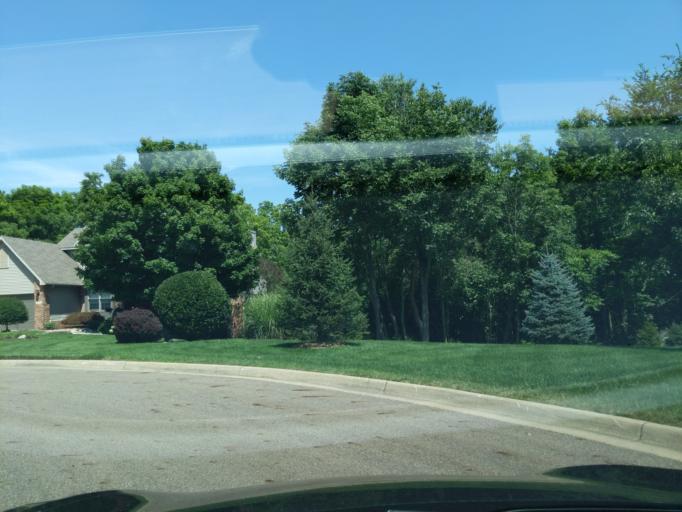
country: US
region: Michigan
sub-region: Ingham County
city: Edgemont Park
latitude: 42.7690
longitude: -84.6112
